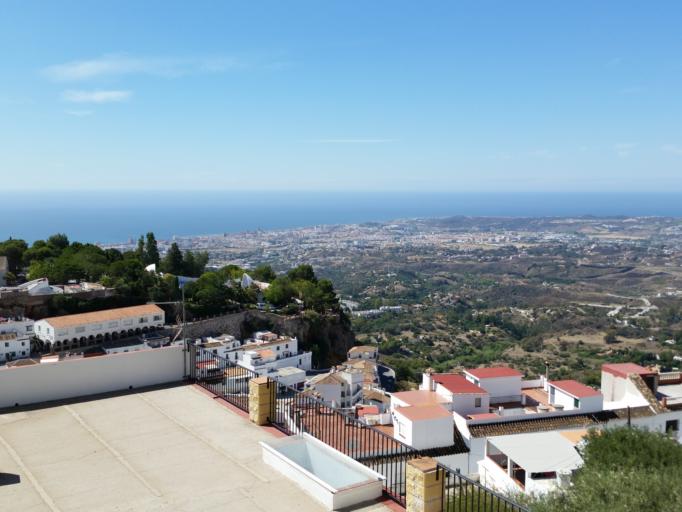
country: ES
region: Andalusia
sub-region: Provincia de Malaga
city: Mijas
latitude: 36.5955
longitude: -4.6409
